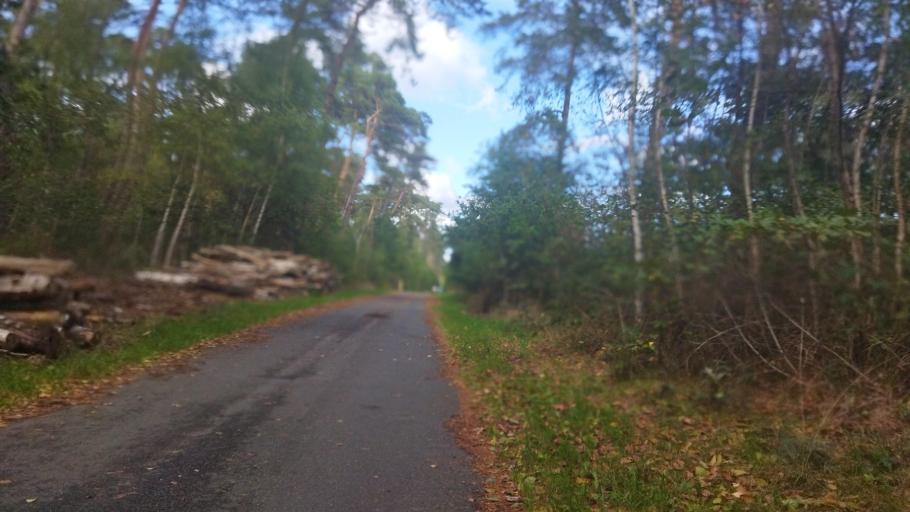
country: DE
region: North Rhine-Westphalia
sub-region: Regierungsbezirk Munster
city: Dulmen
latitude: 51.7912
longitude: 7.2565
